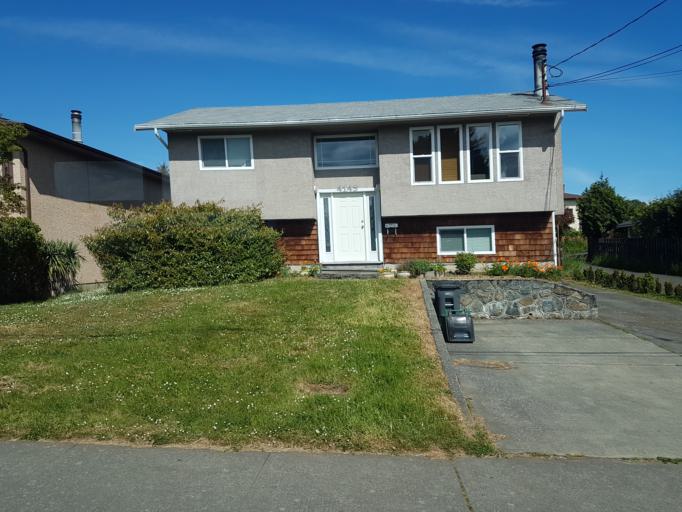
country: CA
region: British Columbia
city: Oak Bay
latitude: 48.4780
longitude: -123.3229
